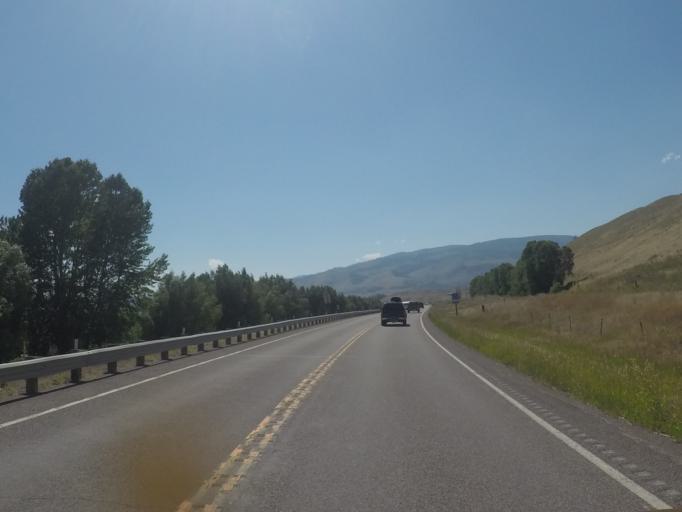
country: US
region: Montana
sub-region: Park County
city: Livingston
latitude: 45.4198
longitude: -110.6667
